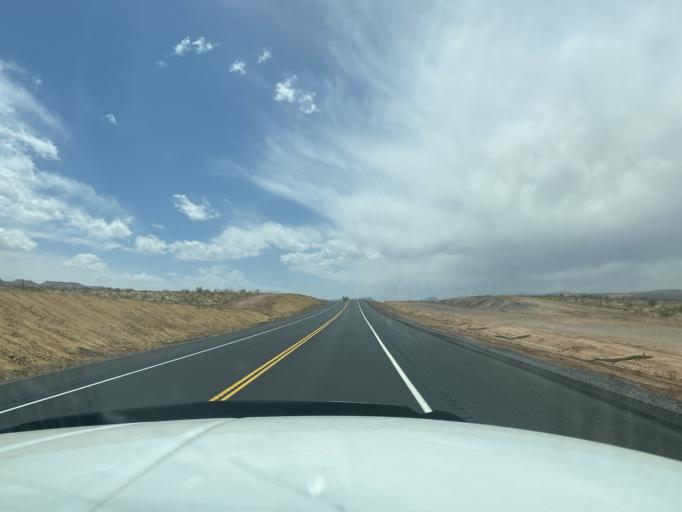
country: US
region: Utah
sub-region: Washington County
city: Hurricane
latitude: 37.1568
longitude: -113.3459
